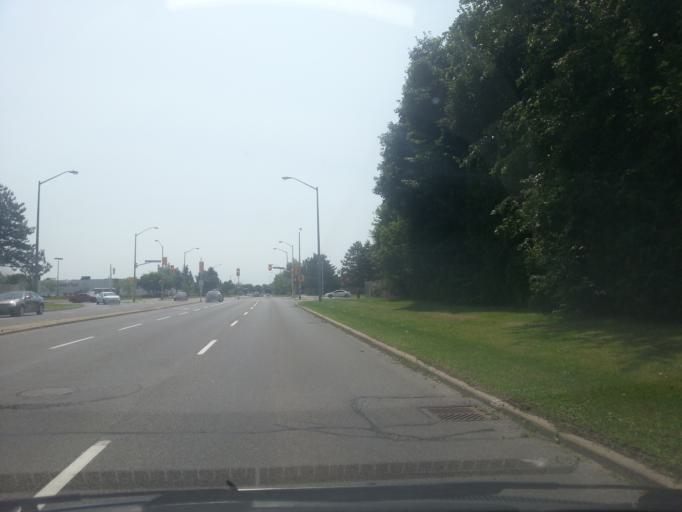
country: CA
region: Quebec
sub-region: Outaouais
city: Gatineau
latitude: 45.4629
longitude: -75.5268
